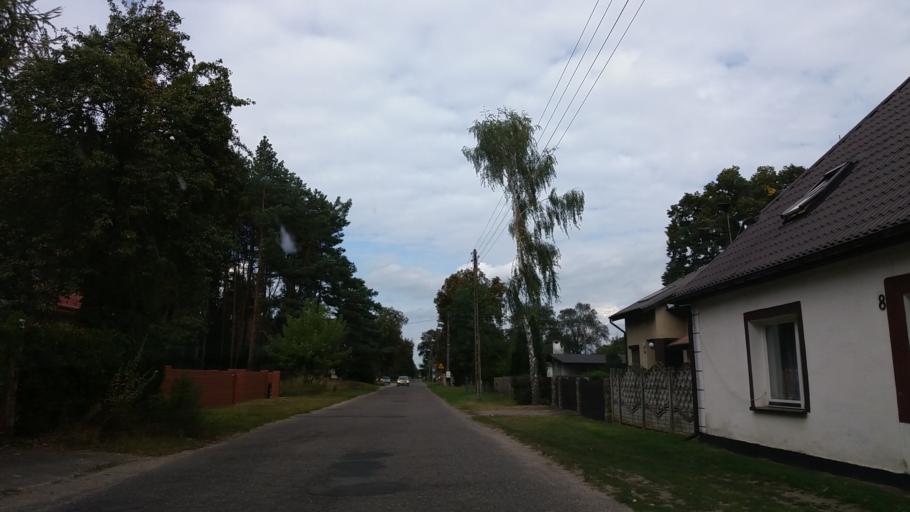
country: PL
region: West Pomeranian Voivodeship
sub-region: Powiat stargardzki
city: Kobylanka
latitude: 53.3354
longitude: 14.8915
